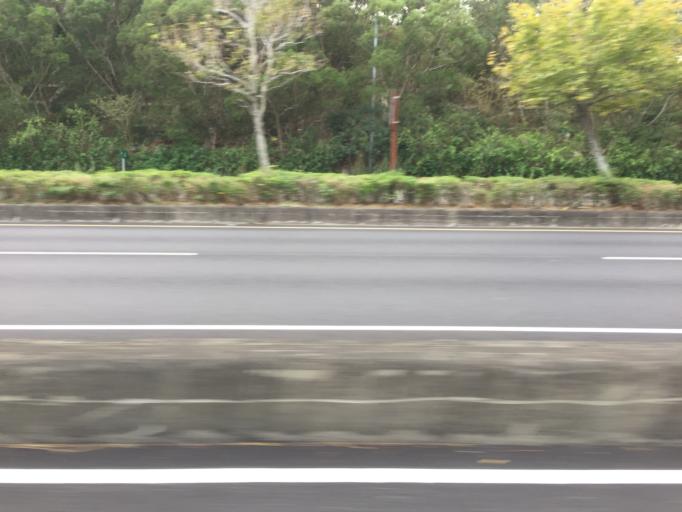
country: TW
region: Taiwan
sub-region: Hsinchu
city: Hsinchu
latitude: 24.7678
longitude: 120.9542
